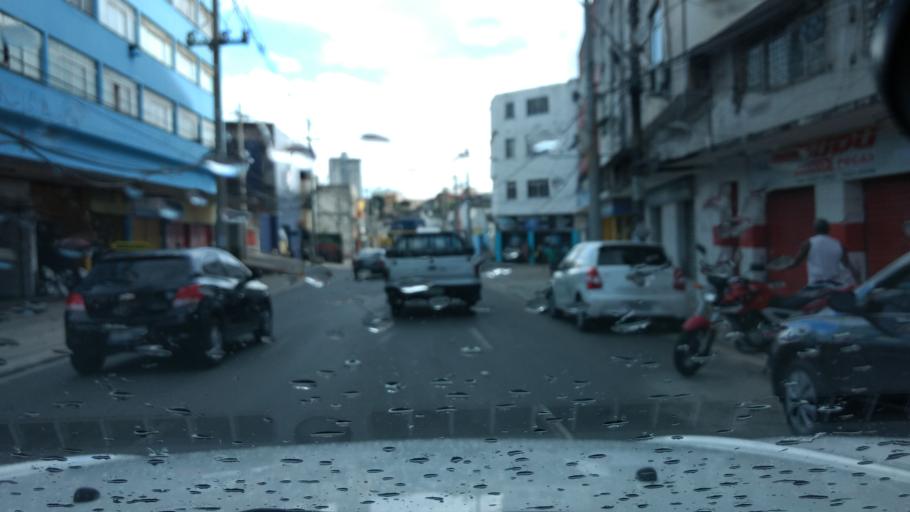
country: BR
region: Bahia
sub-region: Salvador
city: Salvador
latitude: -12.9738
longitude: -38.4997
